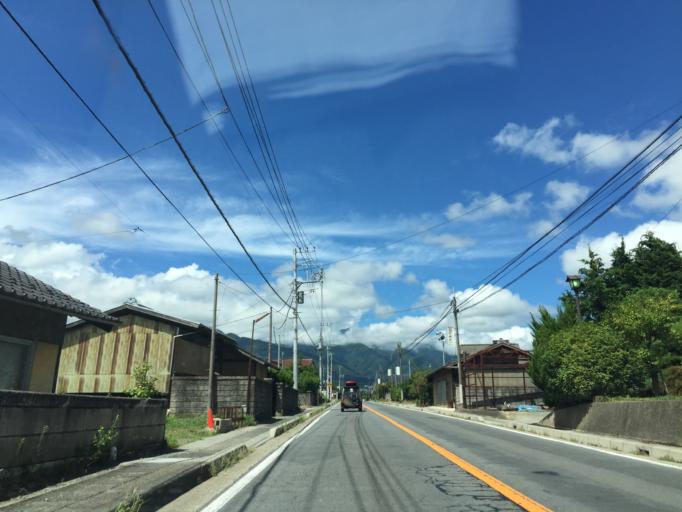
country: JP
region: Yamanashi
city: Nirasaki
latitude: 35.8062
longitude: 138.3505
